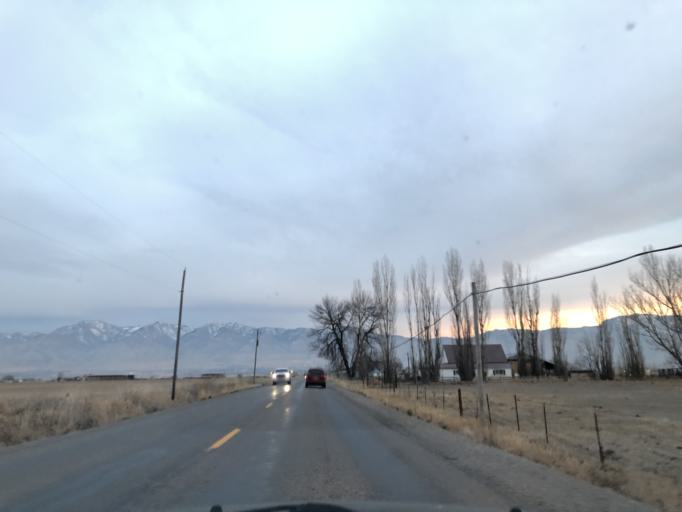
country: US
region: Utah
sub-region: Cache County
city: Benson
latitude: 41.7947
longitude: -111.9019
